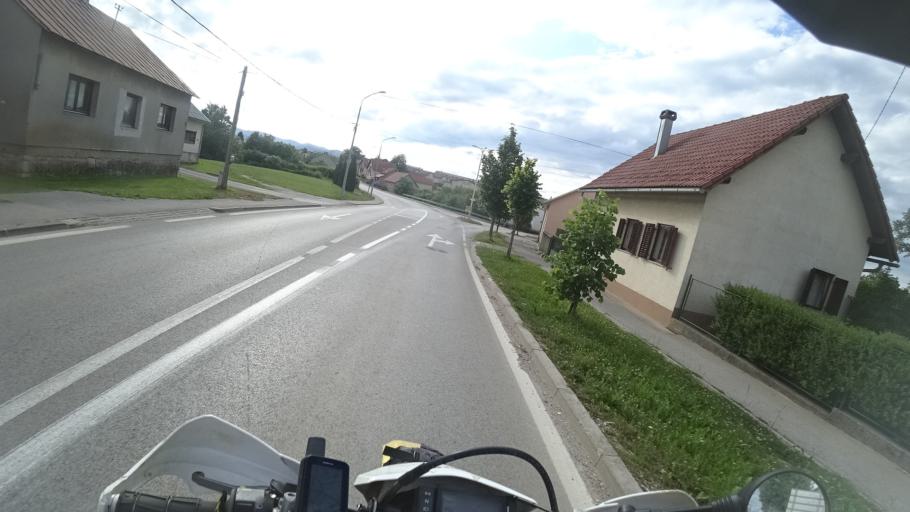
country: HR
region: Licko-Senjska
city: Gospic
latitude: 44.5409
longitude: 15.3806
